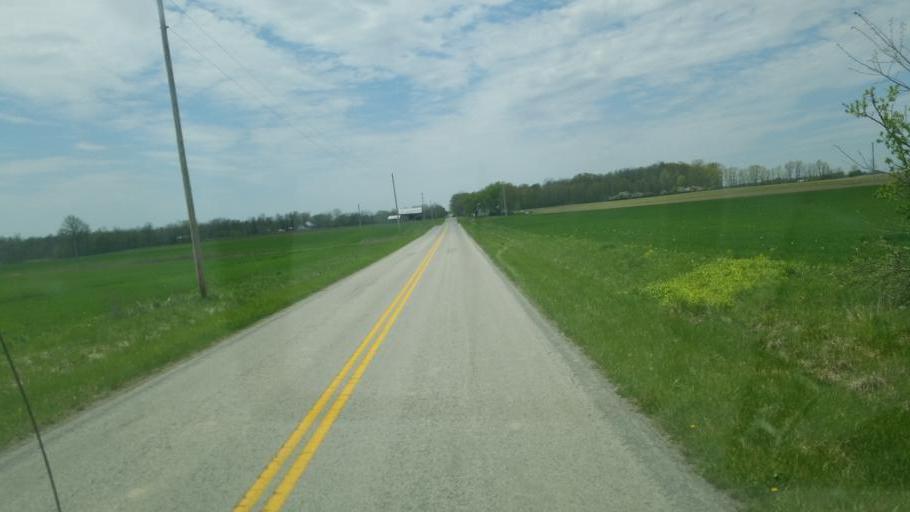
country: US
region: Ohio
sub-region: Hardin County
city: Ada
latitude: 40.7930
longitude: -83.9159
